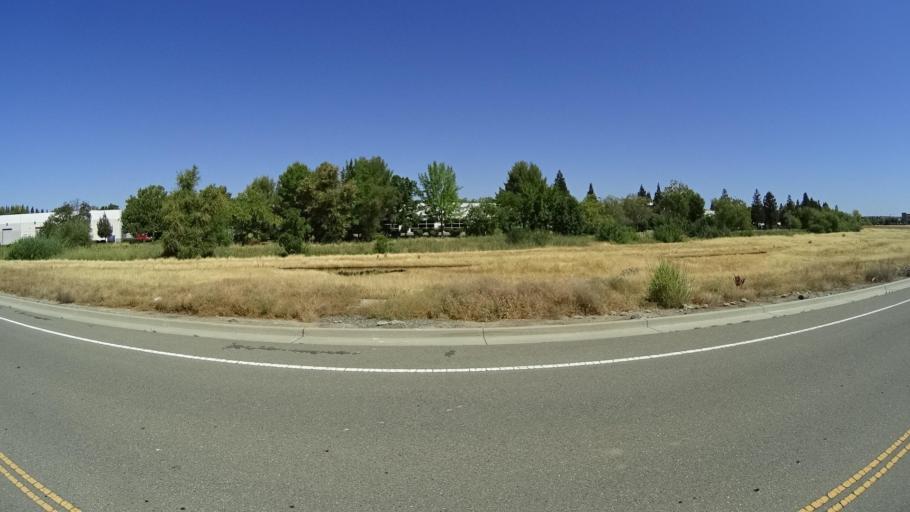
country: US
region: California
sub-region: Placer County
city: Roseville
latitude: 38.8122
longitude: -121.2948
